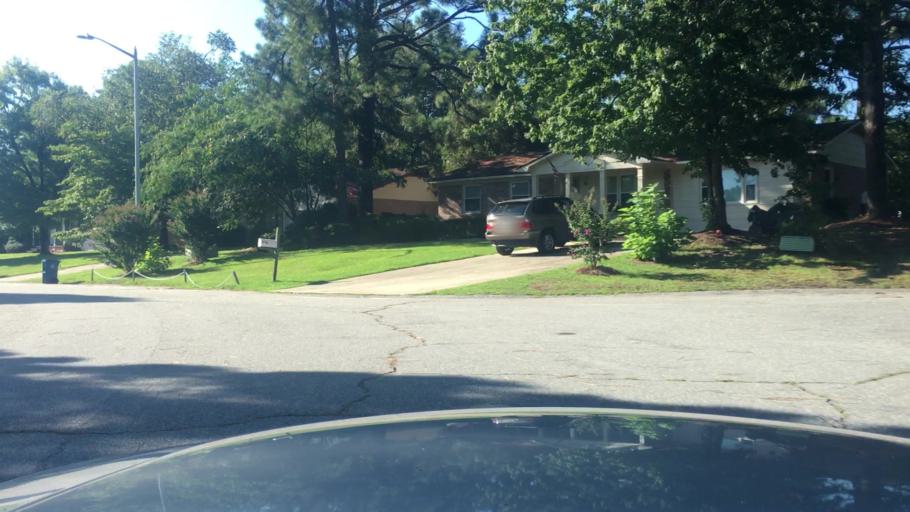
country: US
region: North Carolina
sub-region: Cumberland County
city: Fayetteville
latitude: 35.1370
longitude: -78.8909
